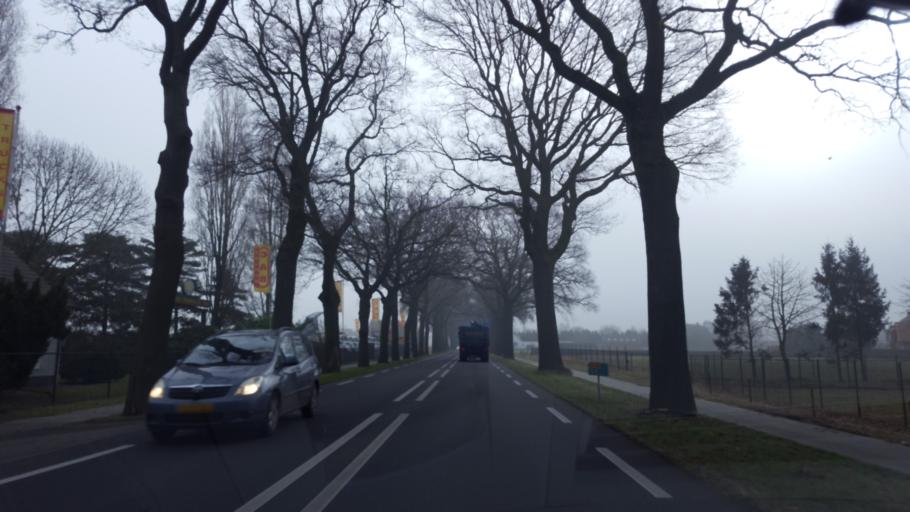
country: NL
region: Limburg
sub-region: Gemeente Nederweert
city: Nederweert
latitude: 51.2416
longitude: 5.7629
